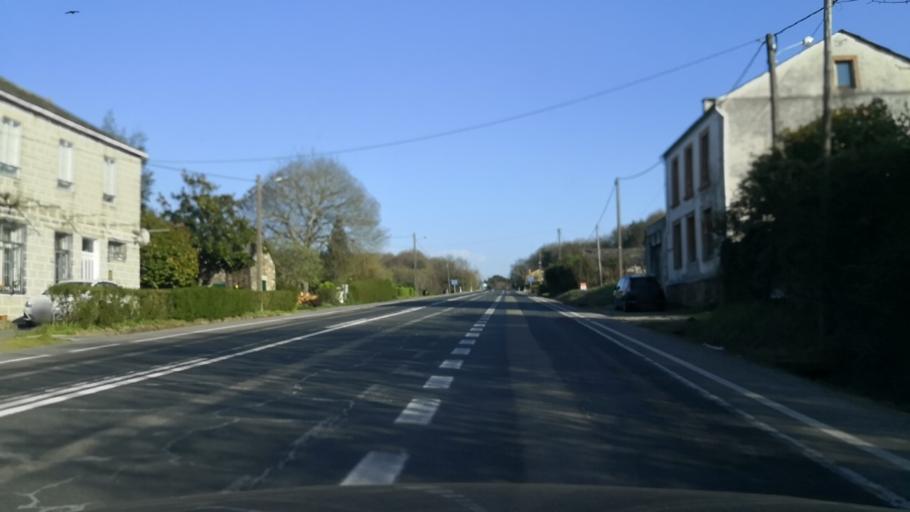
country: ES
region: Galicia
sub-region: Provincia de Lugo
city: Corgo
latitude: 42.9570
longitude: -7.4699
